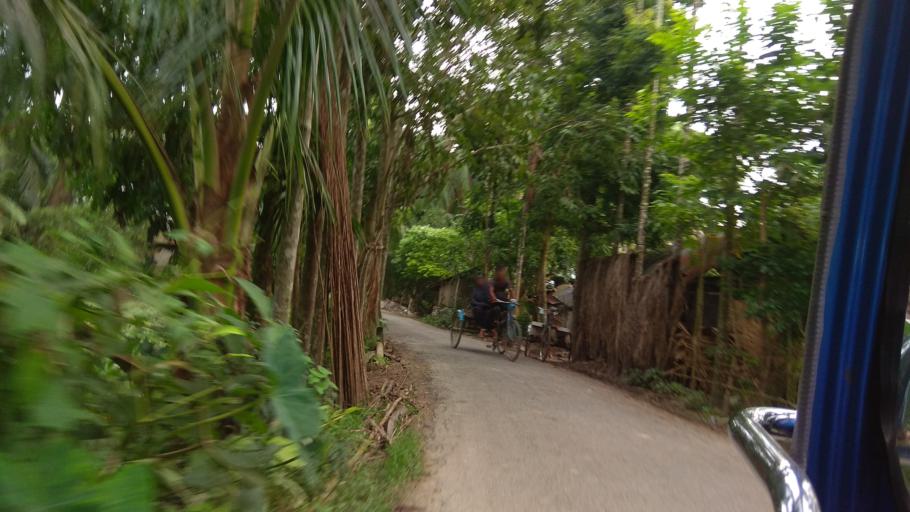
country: BD
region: Khulna
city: Kalia
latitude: 23.0345
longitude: 89.6562
